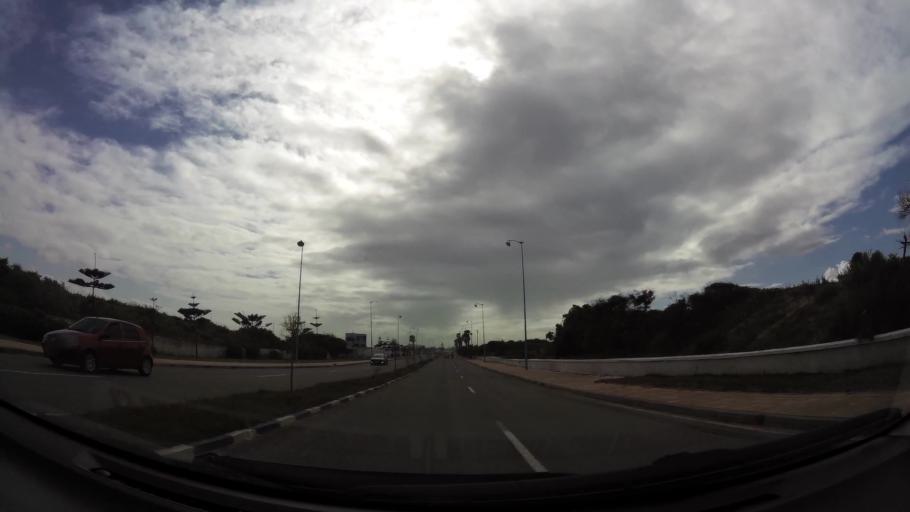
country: MA
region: Doukkala-Abda
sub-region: El-Jadida
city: El Jadida
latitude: 33.2453
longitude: -8.4607
